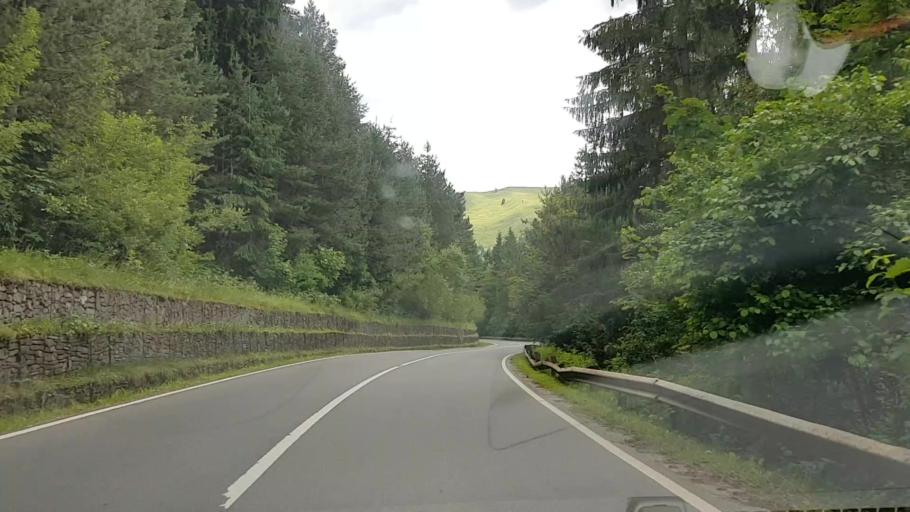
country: RO
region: Neamt
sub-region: Comuna Borca
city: Borca
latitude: 47.1756
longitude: 25.7925
